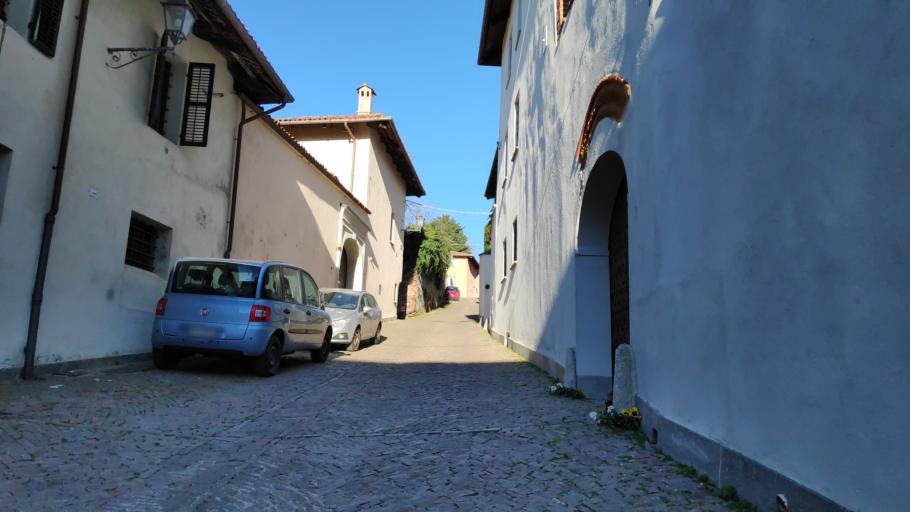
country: IT
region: Piedmont
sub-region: Provincia di Torino
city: Pinerolo
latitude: 44.8871
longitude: 7.3263
